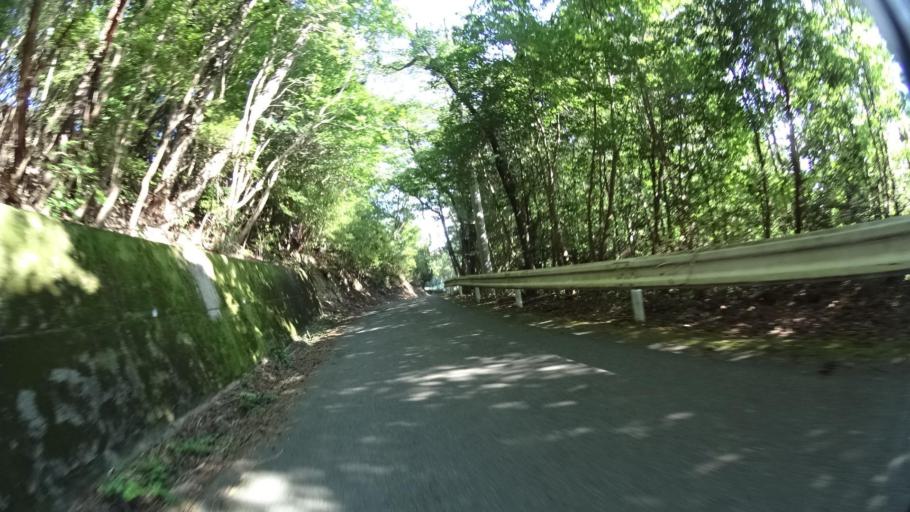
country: JP
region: Kyoto
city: Kameoka
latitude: 34.9814
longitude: 135.5567
